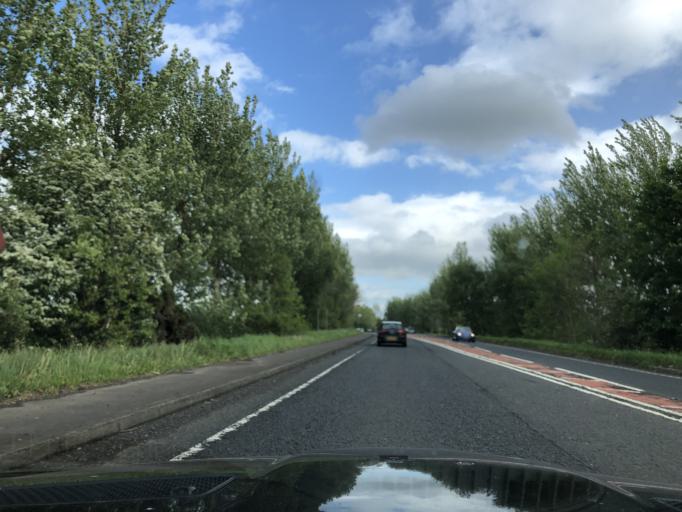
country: GB
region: Northern Ireland
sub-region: Ballymoney District
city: Ballymoney
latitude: 55.0581
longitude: -6.4622
